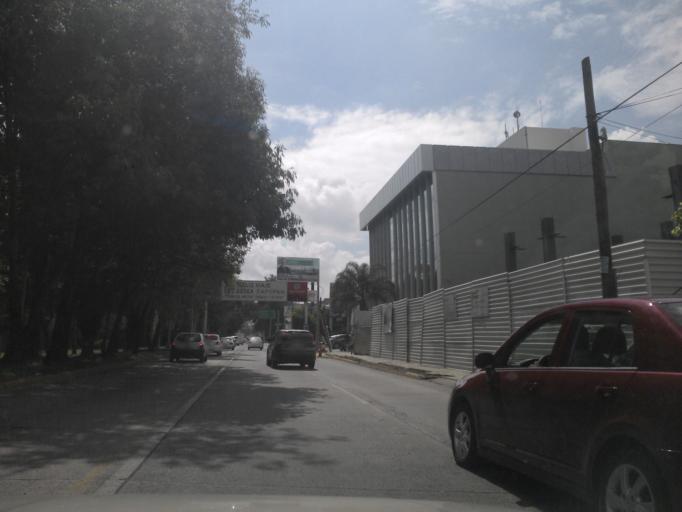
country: MX
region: Jalisco
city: Guadalajara
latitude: 20.6694
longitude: -103.4027
